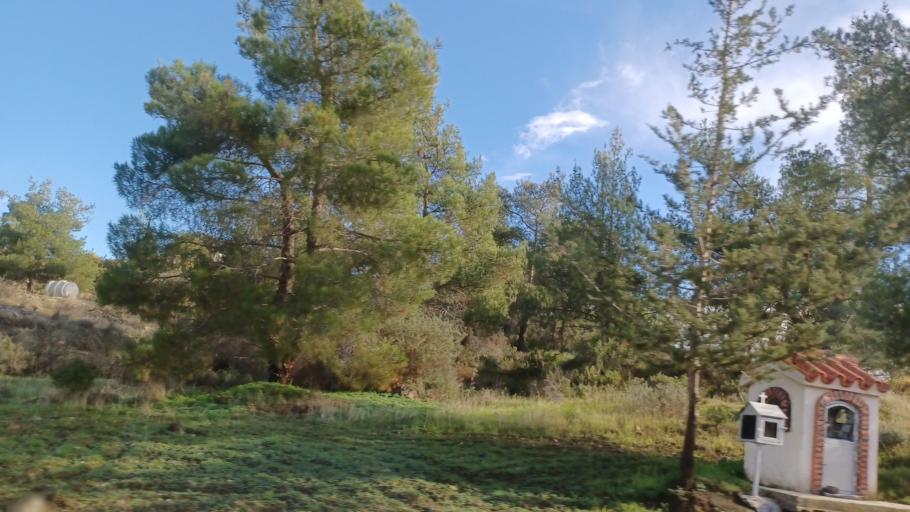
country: CY
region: Lefkosia
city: Lythrodontas
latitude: 34.9430
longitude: 33.2956
